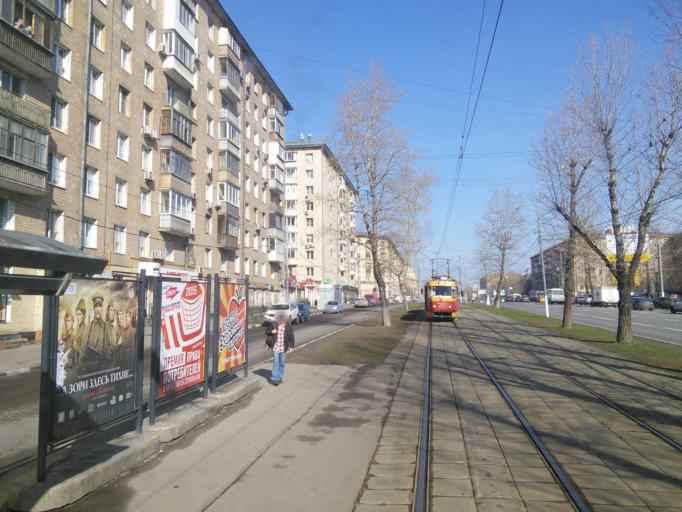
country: RU
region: Moskovskaya
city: Semenovskoye
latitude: 55.6867
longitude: 37.5470
